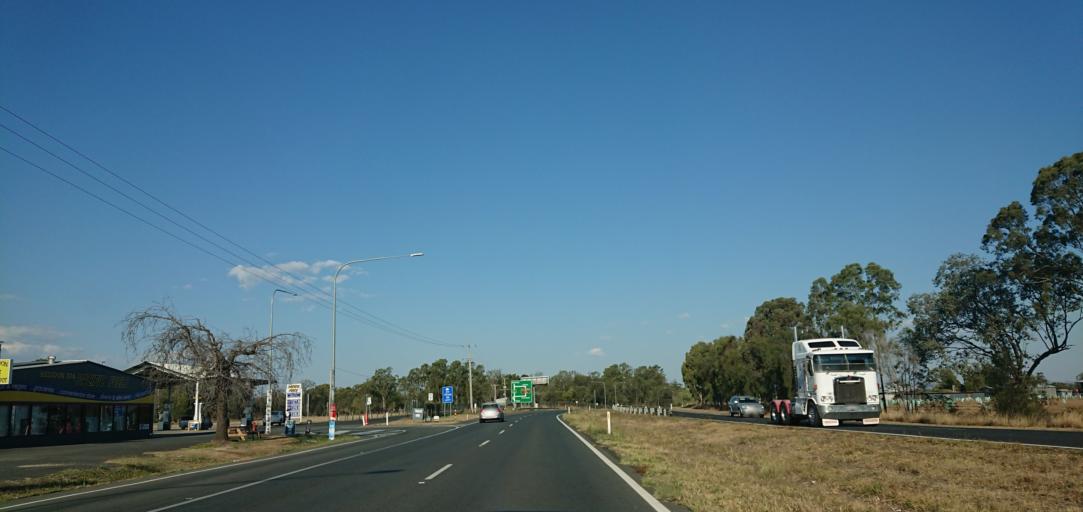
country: AU
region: Queensland
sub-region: Toowoomba
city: Rangeville
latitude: -27.5499
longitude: 152.1151
